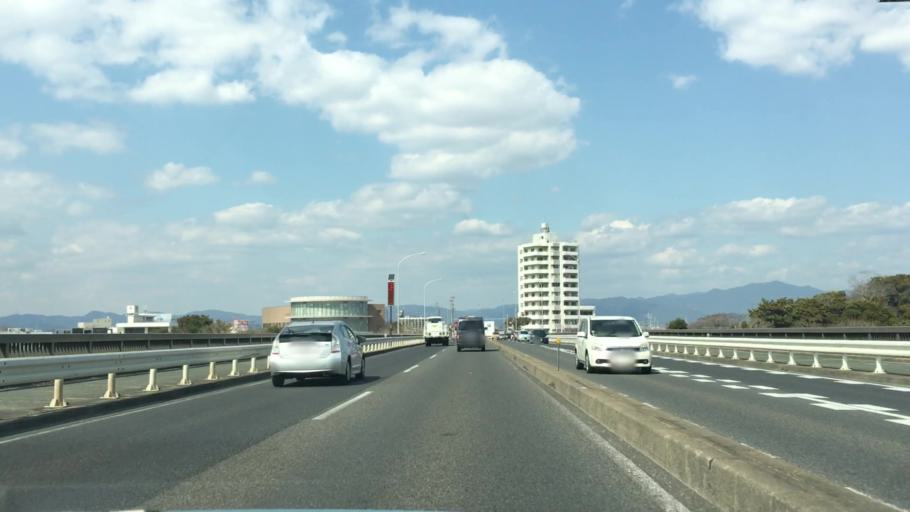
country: JP
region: Aichi
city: Toyohashi
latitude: 34.7710
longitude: 137.3904
